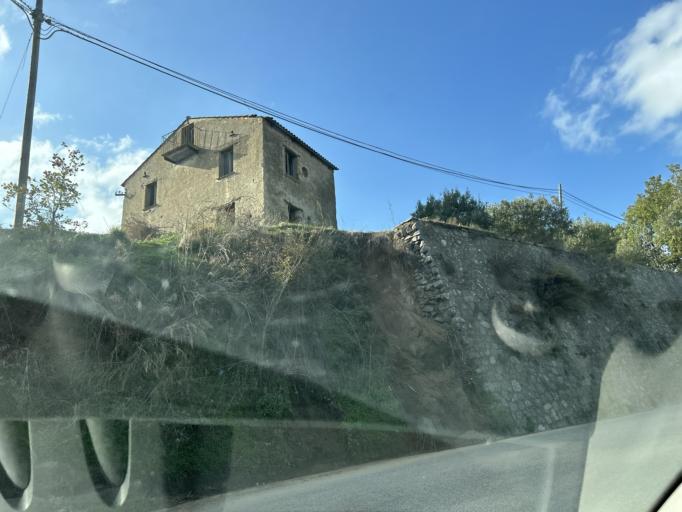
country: IT
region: Calabria
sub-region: Provincia di Catanzaro
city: Montepaone
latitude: 38.7210
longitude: 16.5079
